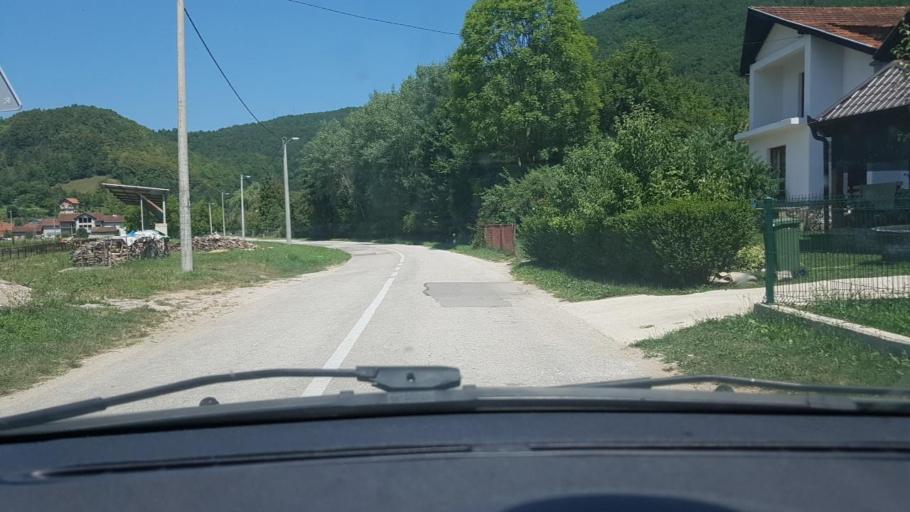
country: BA
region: Federation of Bosnia and Herzegovina
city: Orasac
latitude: 44.5647
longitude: 16.1007
